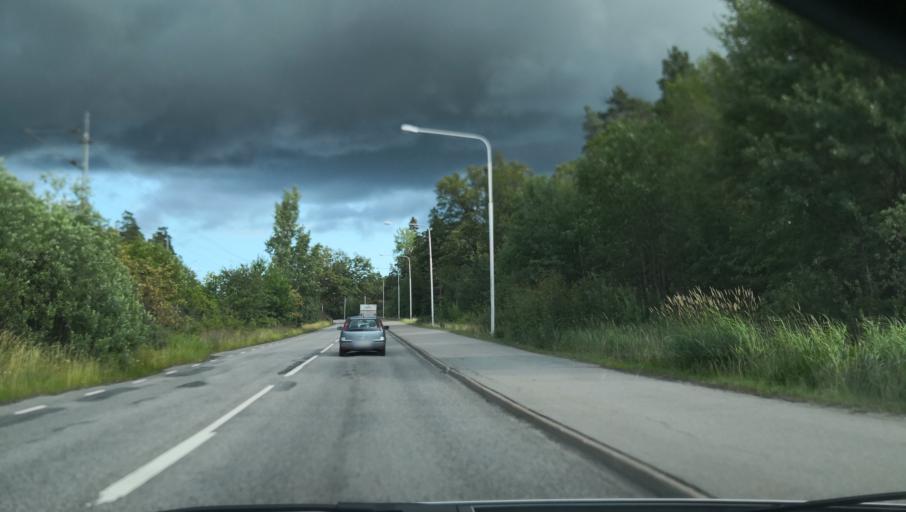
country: SE
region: Stockholm
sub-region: Stockholms Kommun
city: Arsta
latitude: 59.2466
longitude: 18.0670
